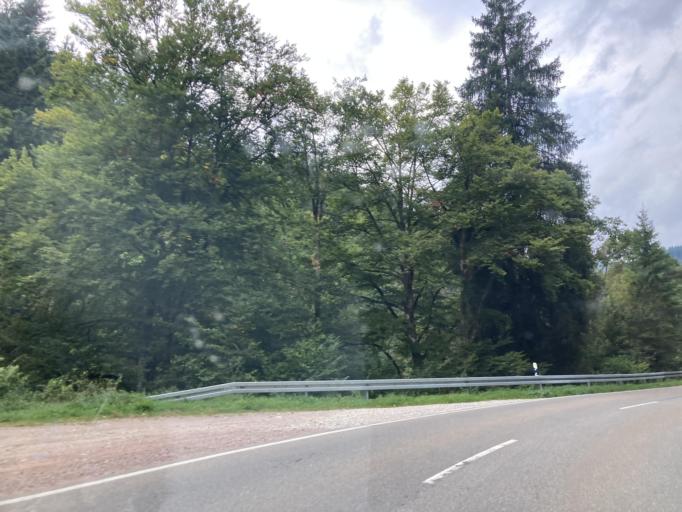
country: DE
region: Baden-Wuerttemberg
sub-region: Freiburg Region
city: Bollen
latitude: 47.7852
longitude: 7.8565
